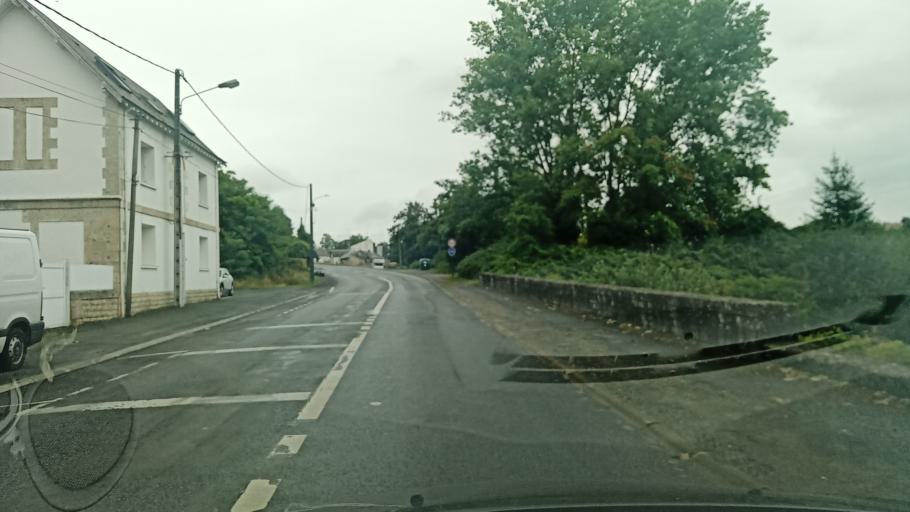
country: FR
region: Poitou-Charentes
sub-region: Departement de la Vienne
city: Poitiers
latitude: 46.6078
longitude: 0.3467
